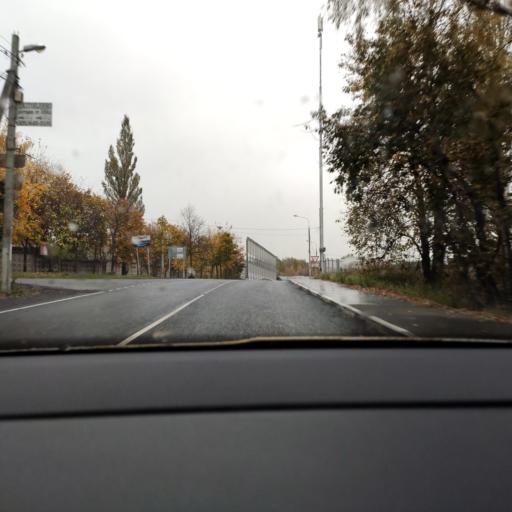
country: RU
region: Moskovskaya
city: Lesnyye Polyany
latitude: 55.9721
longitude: 37.8450
